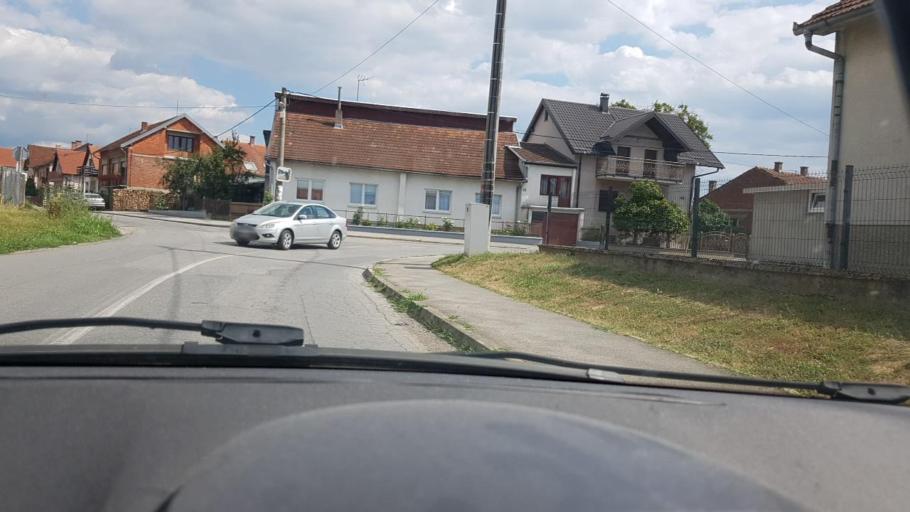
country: HR
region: Bjelovarsko-Bilogorska
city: Bjelovar
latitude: 45.9204
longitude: 16.8479
